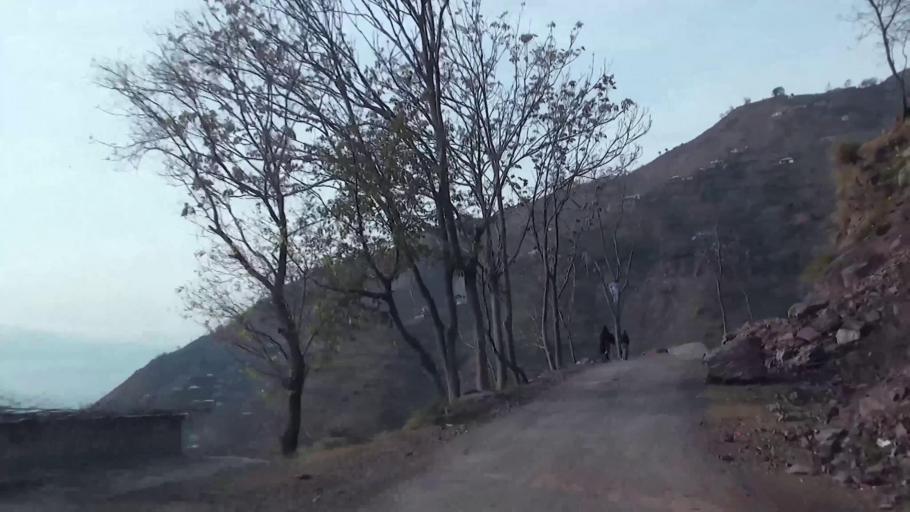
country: PK
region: Azad Kashmir
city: Muzaffarabad
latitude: 34.3676
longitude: 73.5257
